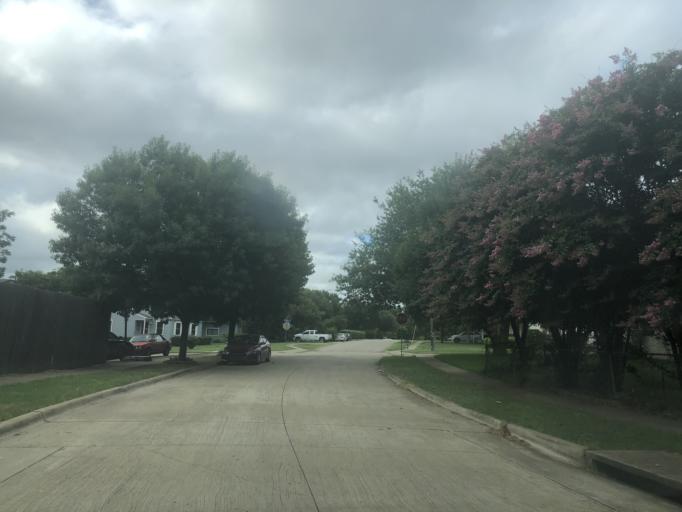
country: US
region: Texas
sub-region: Dallas County
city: Duncanville
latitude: 32.6551
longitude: -96.9054
